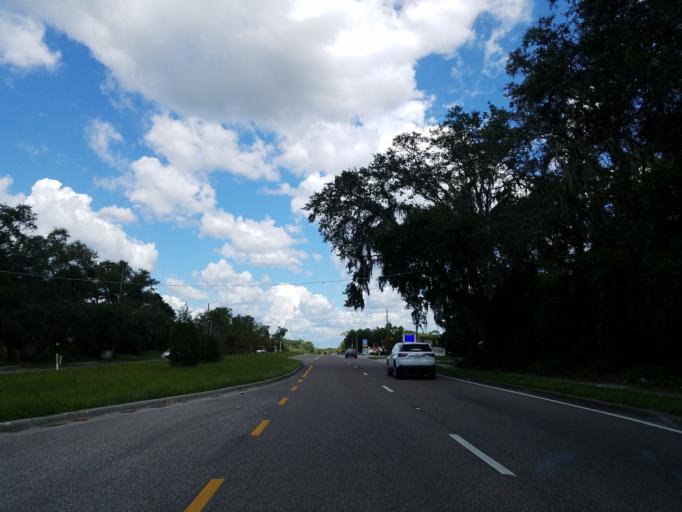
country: US
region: Florida
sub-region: Hillsborough County
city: Citrus Park
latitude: 28.0655
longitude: -82.5636
